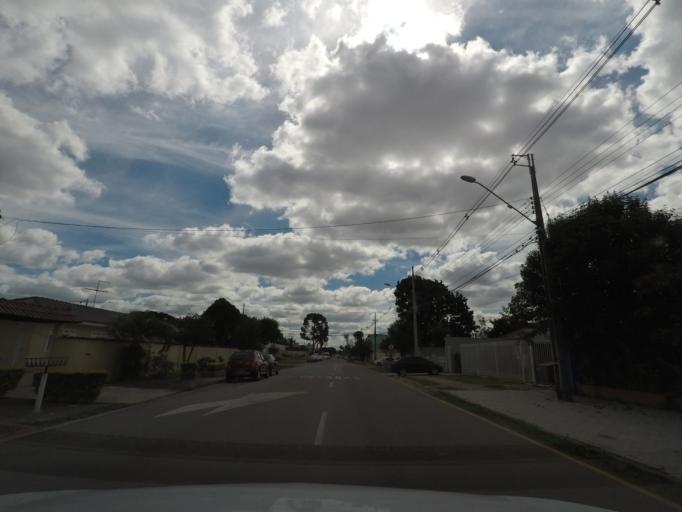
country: BR
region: Parana
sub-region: Sao Jose Dos Pinhais
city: Sao Jose dos Pinhais
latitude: -25.4930
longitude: -49.2377
